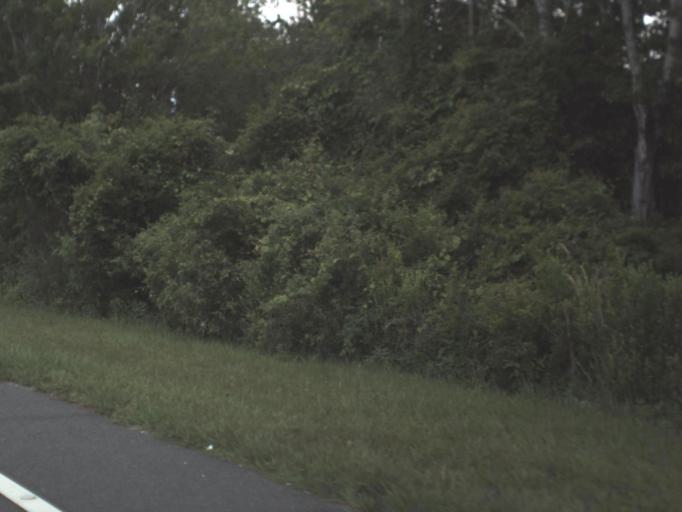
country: US
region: Florida
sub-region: Levy County
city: Chiefland
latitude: 29.1987
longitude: -82.9960
